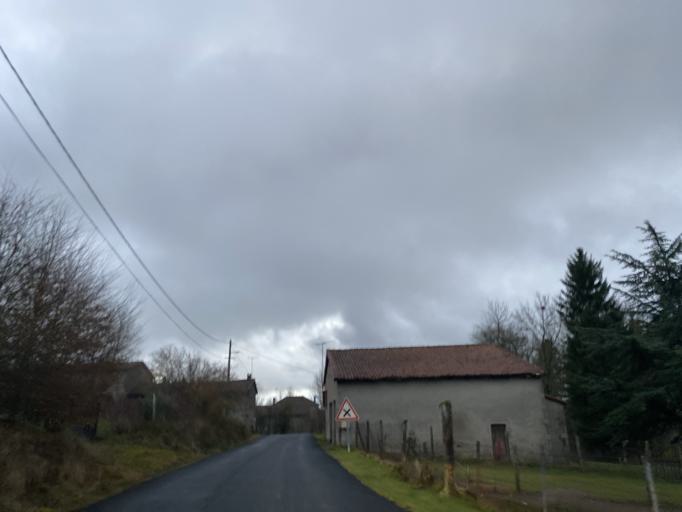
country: FR
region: Auvergne
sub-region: Departement du Puy-de-Dome
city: Cunlhat
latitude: 45.5612
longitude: 3.5730
